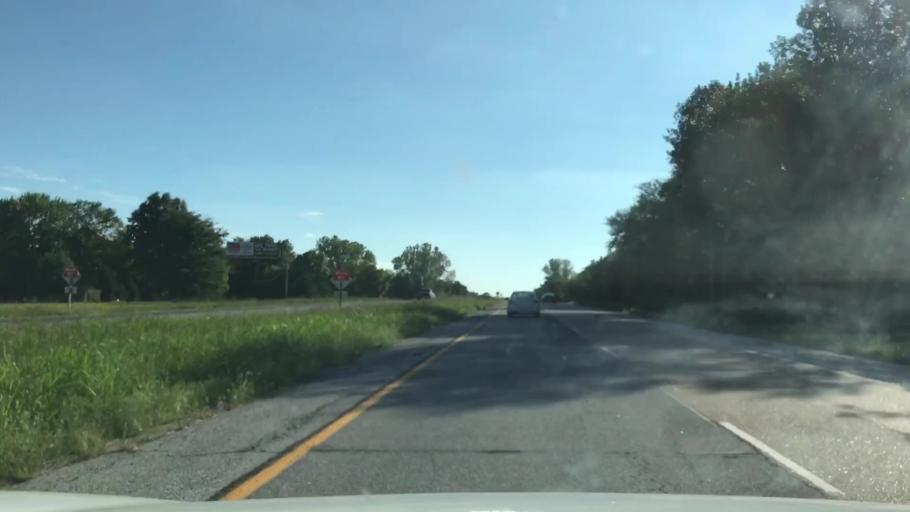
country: US
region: Illinois
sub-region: Madison County
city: Mitchell
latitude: 38.7791
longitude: -90.1119
